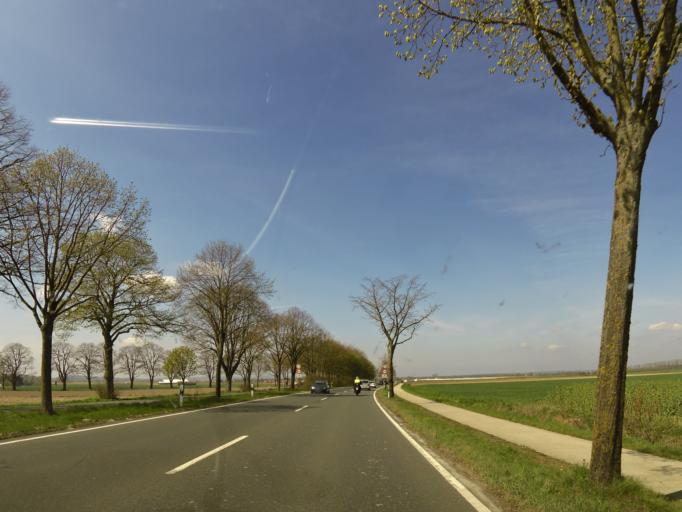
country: DE
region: Lower Saxony
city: Hagenburg
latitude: 52.4334
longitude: 9.3756
